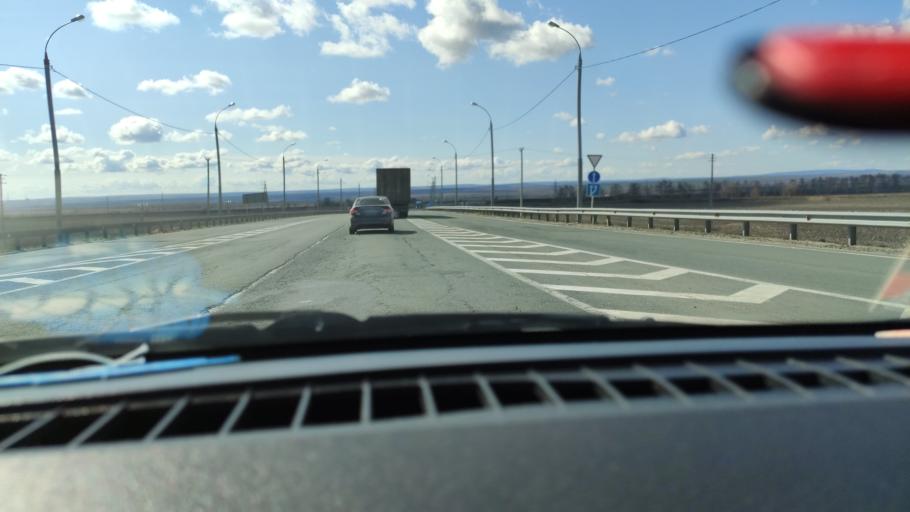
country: RU
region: Samara
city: Varlamovo
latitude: 53.1893
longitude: 48.2920
